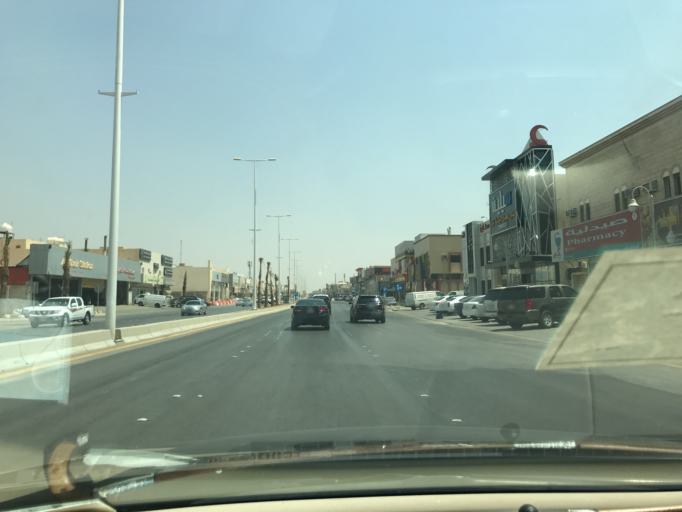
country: SA
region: Ar Riyad
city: Riyadh
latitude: 24.7490
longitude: 46.7635
